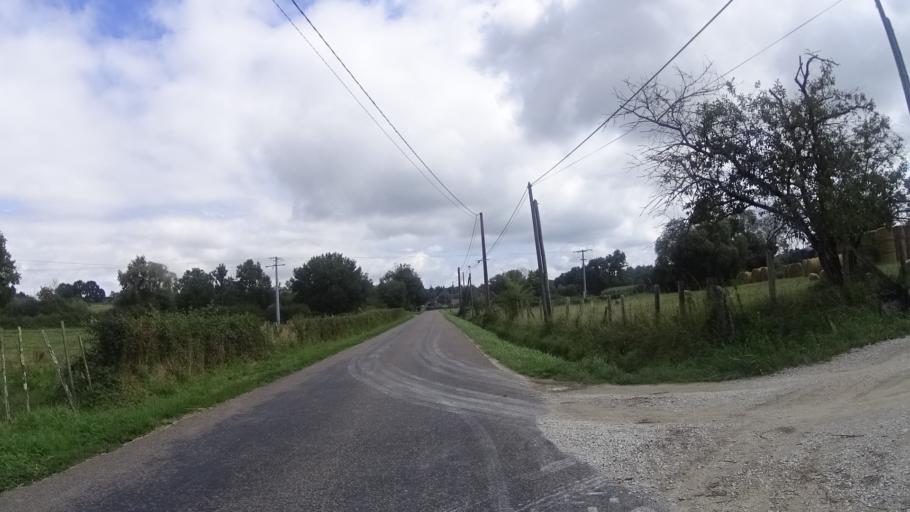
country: FR
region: Champagne-Ardenne
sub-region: Departement de l'Aube
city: Ervy-le-Chatel
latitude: 48.0731
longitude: 3.9604
